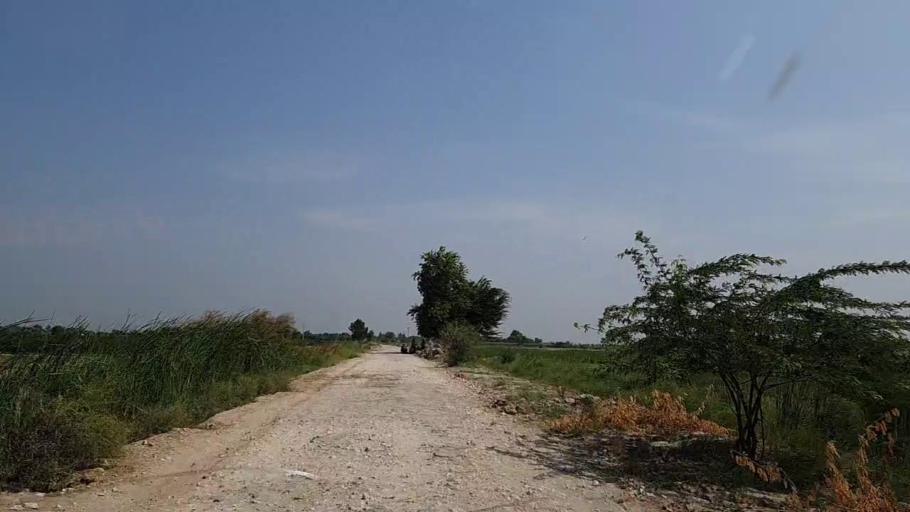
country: PK
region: Sindh
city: Khanpur
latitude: 27.7930
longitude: 69.3164
